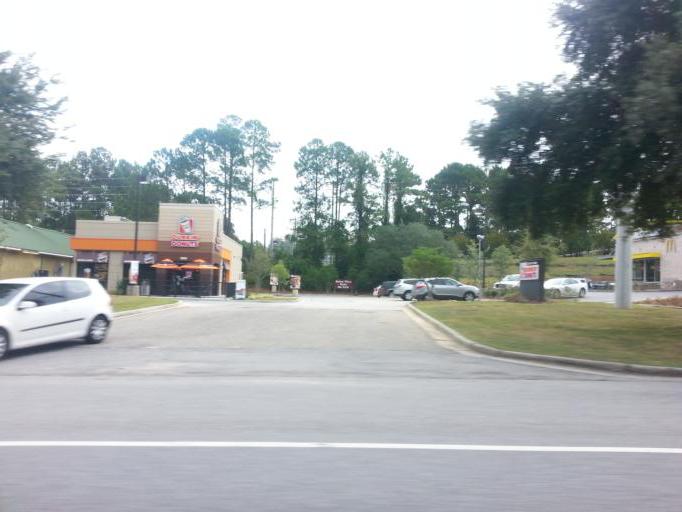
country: US
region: Alabama
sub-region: Baldwin County
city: Spanish Fort
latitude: 30.6501
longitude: -87.9124
